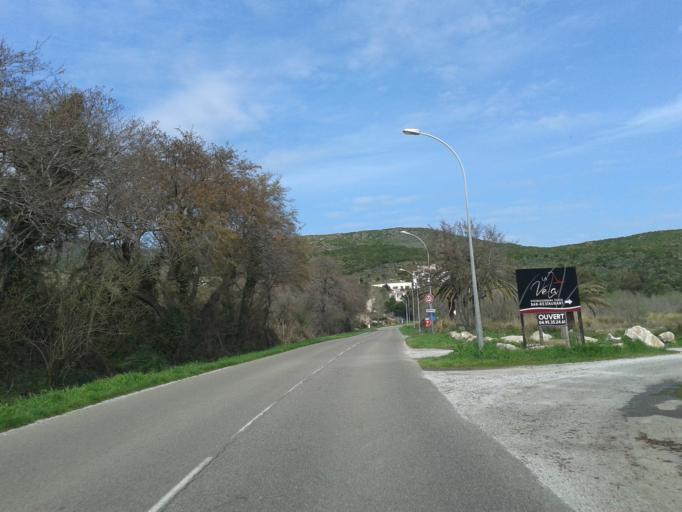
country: FR
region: Corsica
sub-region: Departement de la Haute-Corse
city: Brando
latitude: 42.8388
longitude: 9.4782
